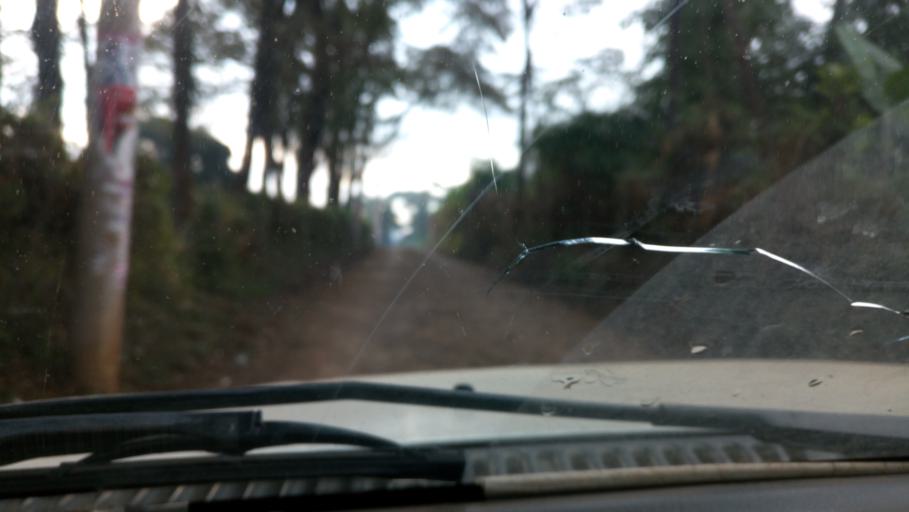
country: KE
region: Kiambu
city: Kikuyu
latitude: -1.2744
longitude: 36.7088
